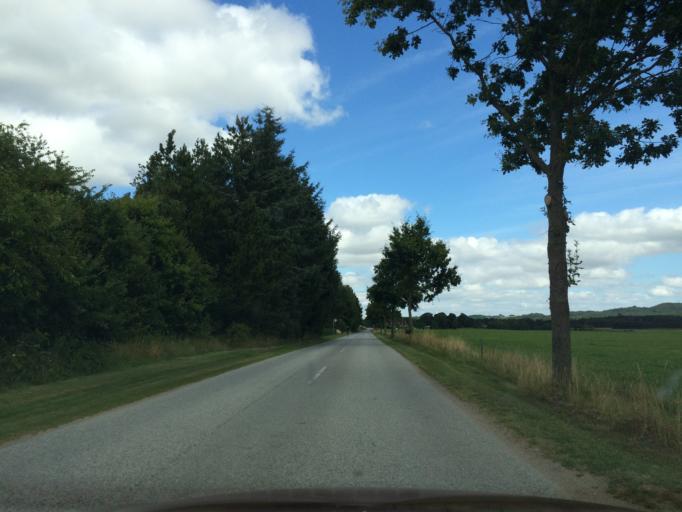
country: DK
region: Central Jutland
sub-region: Silkeborg Kommune
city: Svejbaek
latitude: 56.2176
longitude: 9.6617
